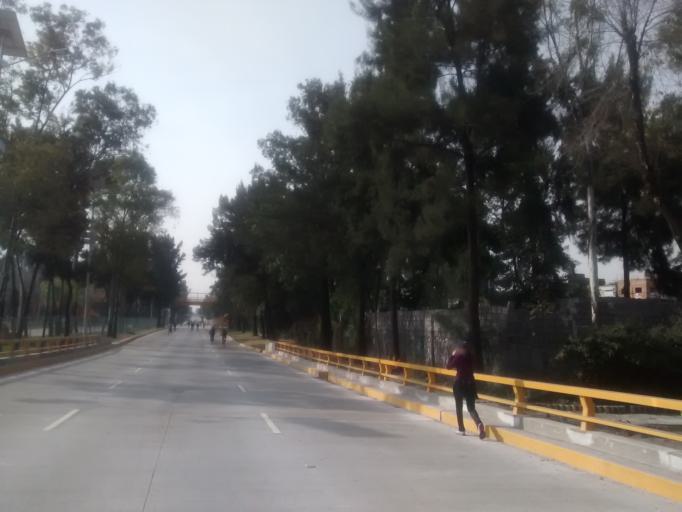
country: MX
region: Mexico City
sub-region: Iztacalco
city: Iztacalco
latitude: 19.3941
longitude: -99.0993
